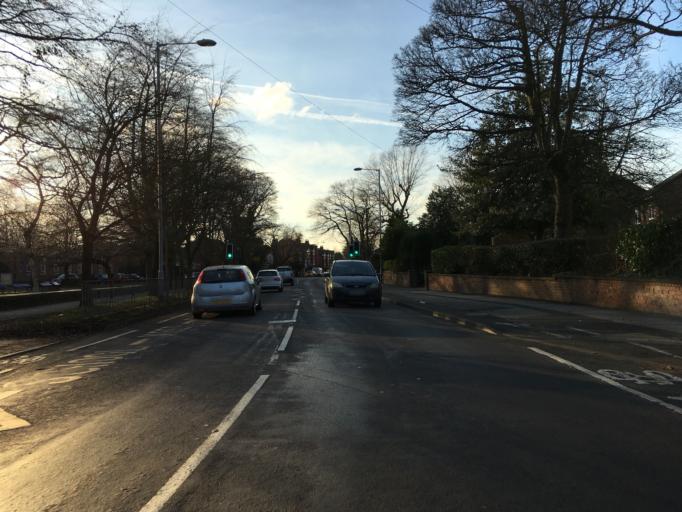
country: GB
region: England
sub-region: Borough of Stockport
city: Cheadle Heath
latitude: 53.4134
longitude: -2.1999
